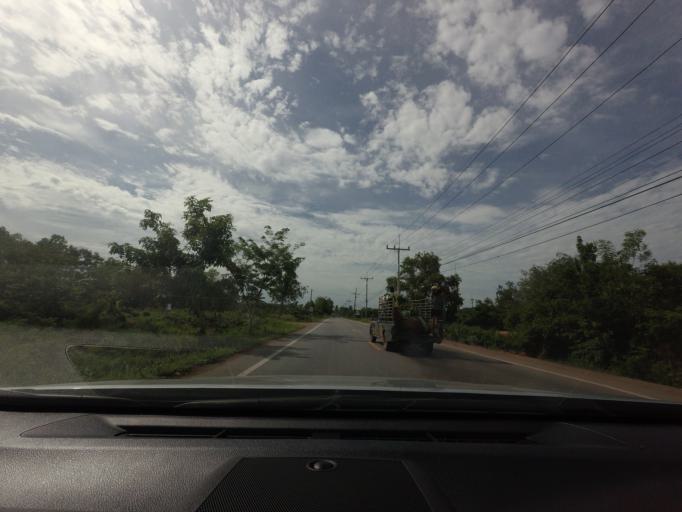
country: TH
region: Songkhla
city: Khlong Hoi Khong
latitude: 6.8869
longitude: 100.4156
